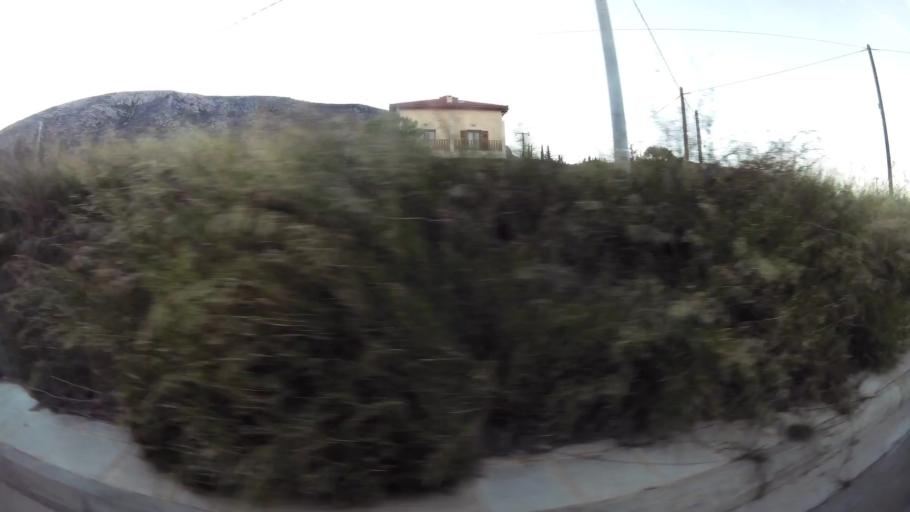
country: GR
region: Attica
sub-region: Nomarchia Anatolikis Attikis
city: Paiania
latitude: 37.9573
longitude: 23.8450
